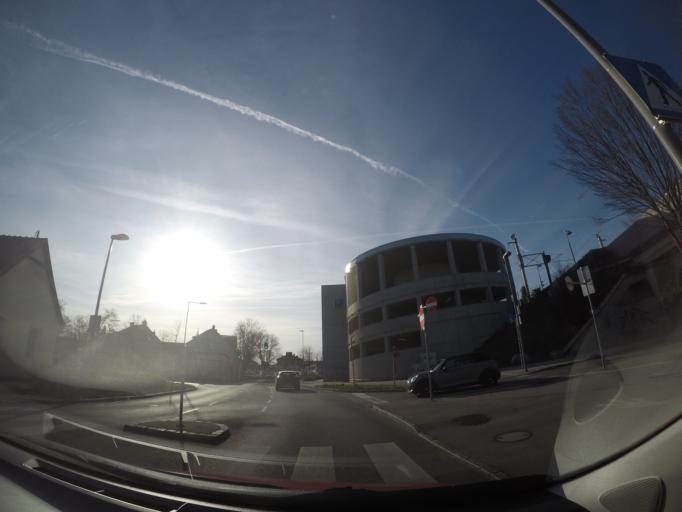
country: AT
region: Lower Austria
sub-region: Politischer Bezirk Baden
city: Baden
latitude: 48.0053
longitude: 16.2445
